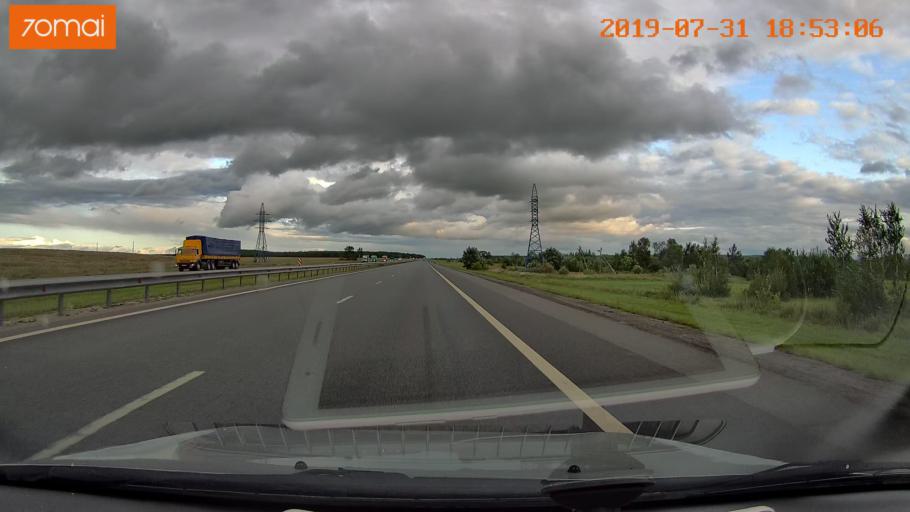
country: RU
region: Moskovskaya
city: Raduzhnyy
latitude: 55.2067
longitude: 38.6461
